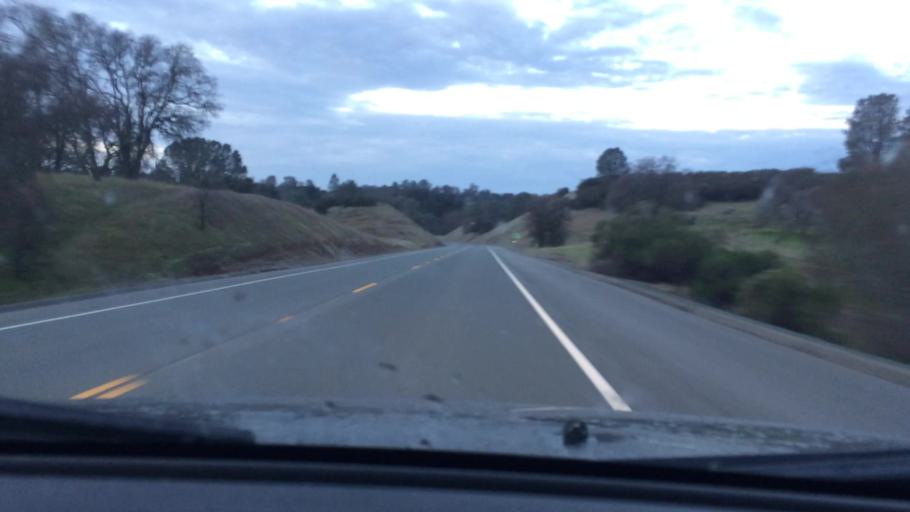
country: US
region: California
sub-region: Amador County
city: Ione
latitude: 38.4101
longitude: -120.8877
